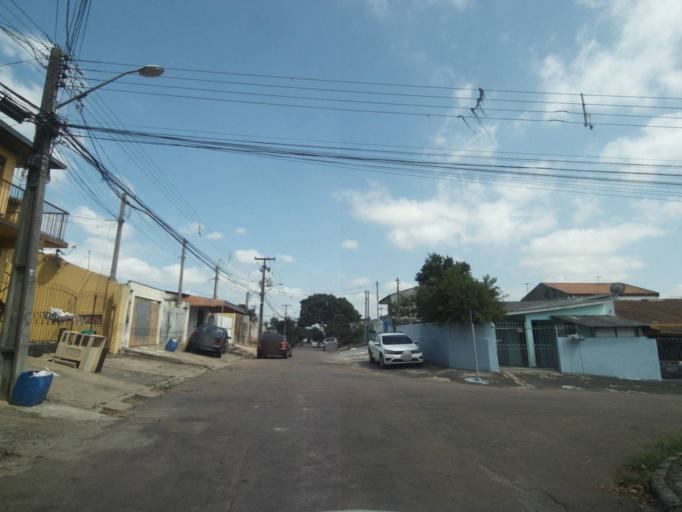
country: BR
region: Parana
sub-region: Sao Jose Dos Pinhais
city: Sao Jose dos Pinhais
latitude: -25.5429
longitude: -49.2659
